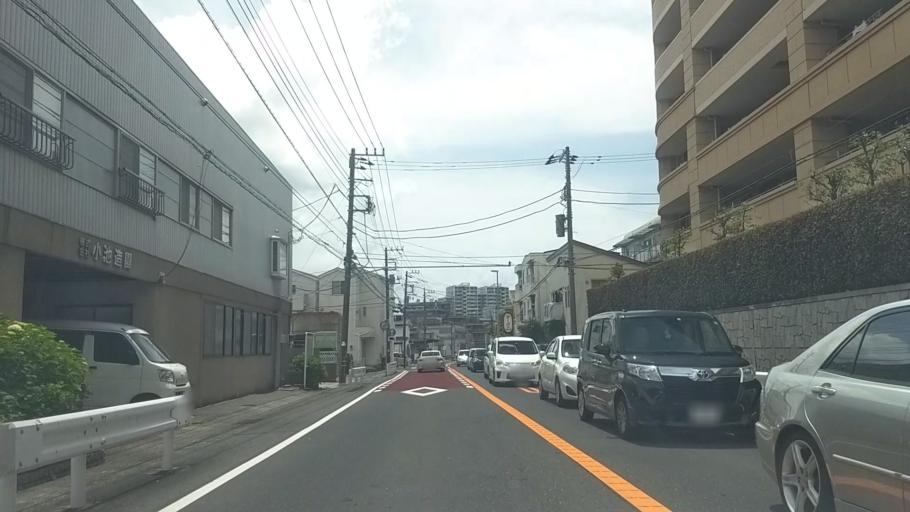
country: JP
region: Kanagawa
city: Fujisawa
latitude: 35.3478
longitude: 139.4937
